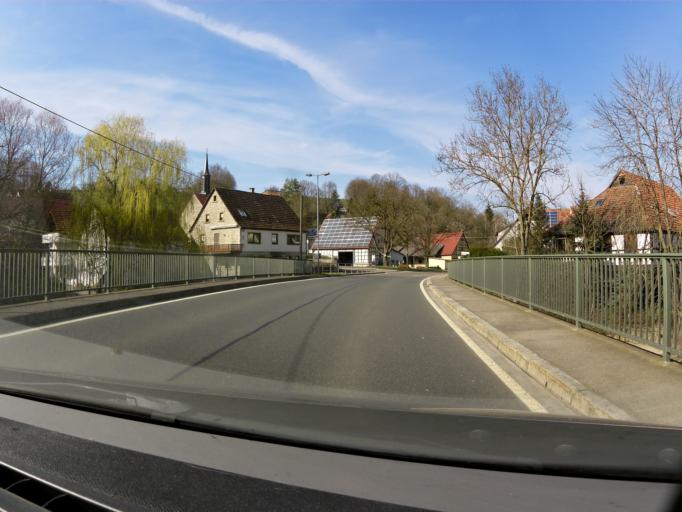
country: DE
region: Baden-Wuerttemberg
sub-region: Regierungsbezirk Stuttgart
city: Creglingen
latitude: 49.4914
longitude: 10.0172
